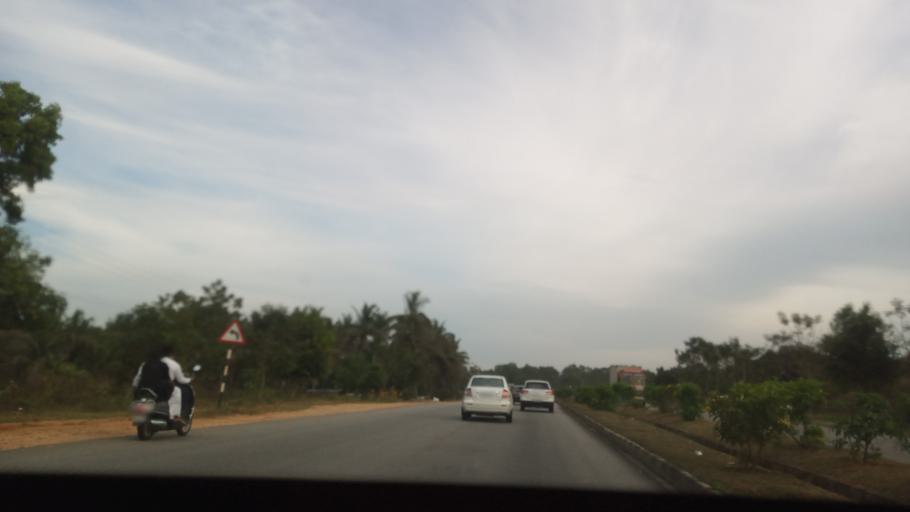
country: IN
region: Karnataka
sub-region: Ramanagara
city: Magadi
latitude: 13.0744
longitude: 77.2172
